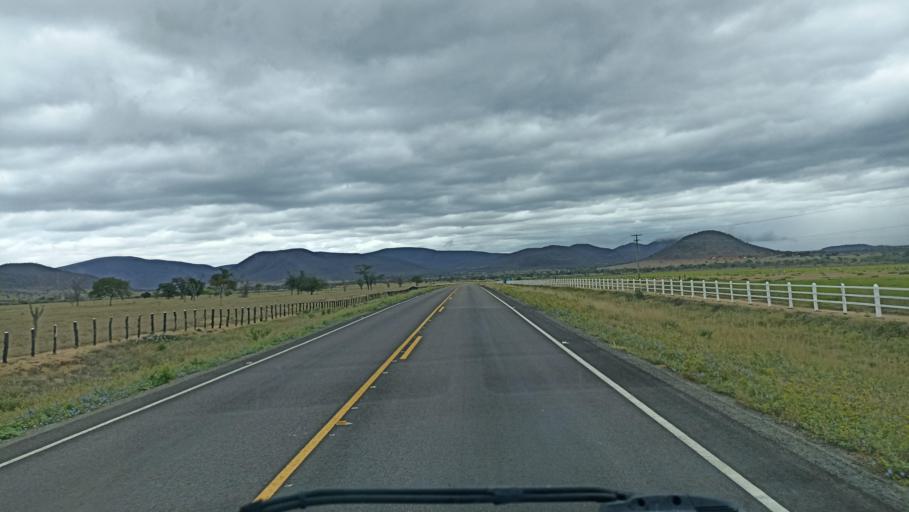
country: BR
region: Bahia
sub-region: Iacu
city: Iacu
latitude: -12.9168
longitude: -40.4121
